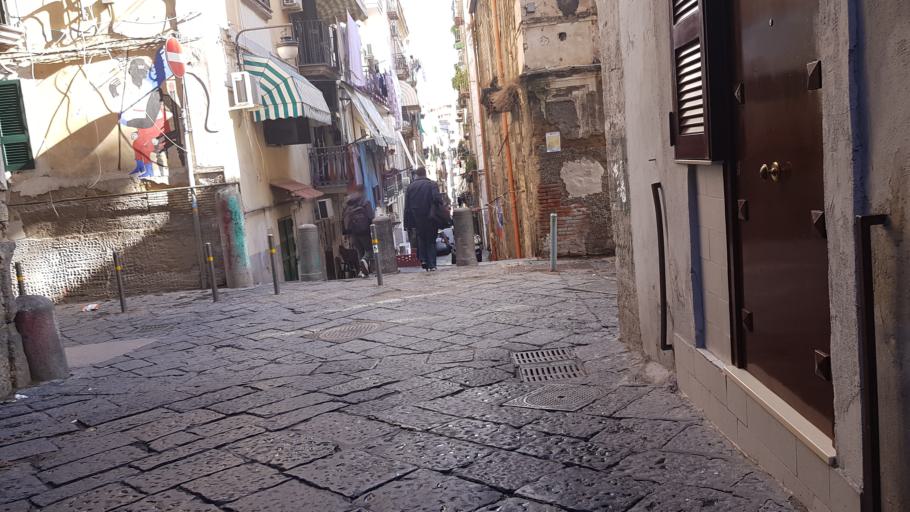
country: IT
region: Campania
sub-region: Provincia di Napoli
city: Napoli
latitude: 40.8418
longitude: 14.2463
